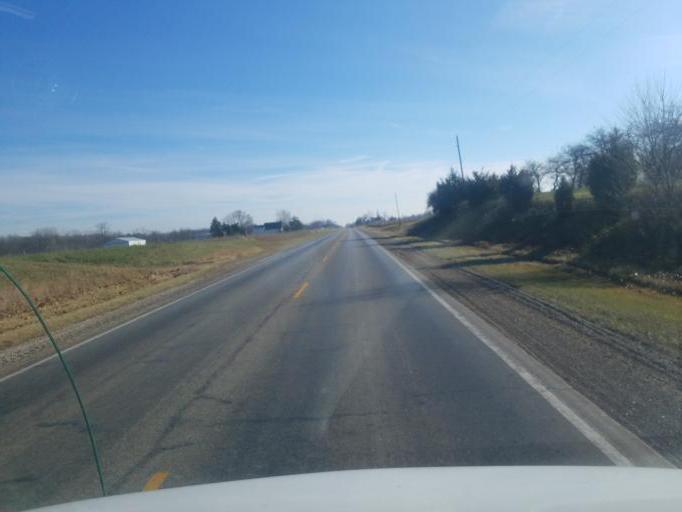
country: US
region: Indiana
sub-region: Adams County
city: Geneva
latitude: 40.5414
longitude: -84.9379
